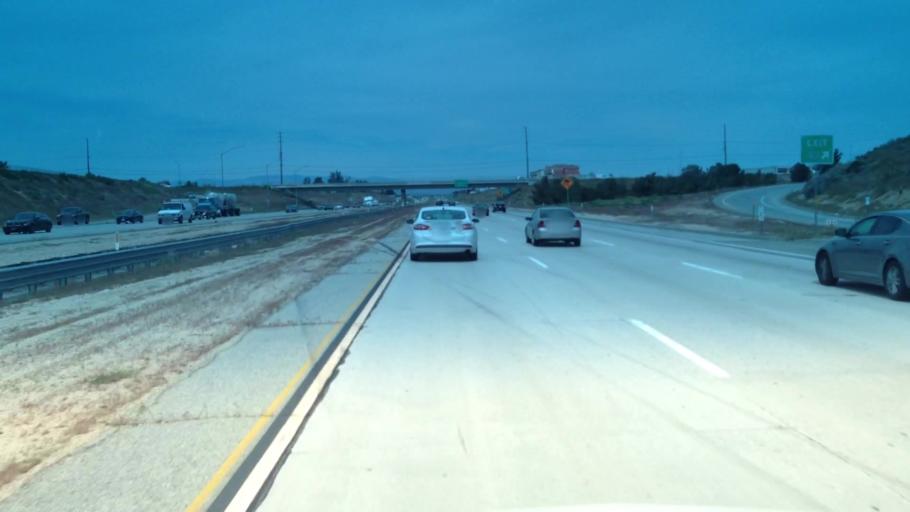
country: US
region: California
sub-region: Los Angeles County
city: Desert View Highlands
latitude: 34.6429
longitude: -118.1527
